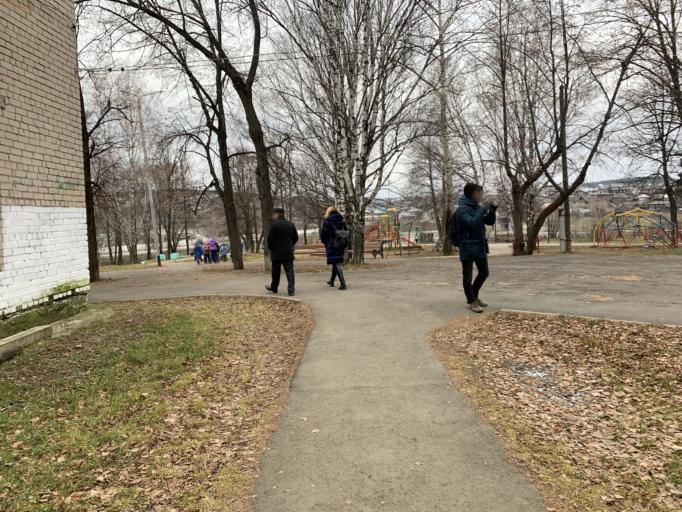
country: RU
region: Chelyabinsk
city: Nyazepetrovsk
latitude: 56.0549
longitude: 59.5956
